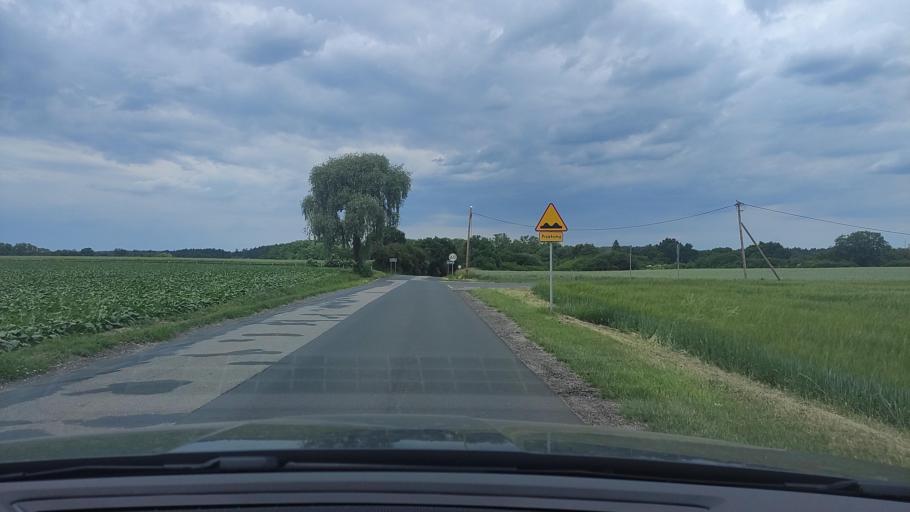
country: PL
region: Greater Poland Voivodeship
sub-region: Powiat poznanski
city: Kostrzyn
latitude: 52.4448
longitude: 17.1689
